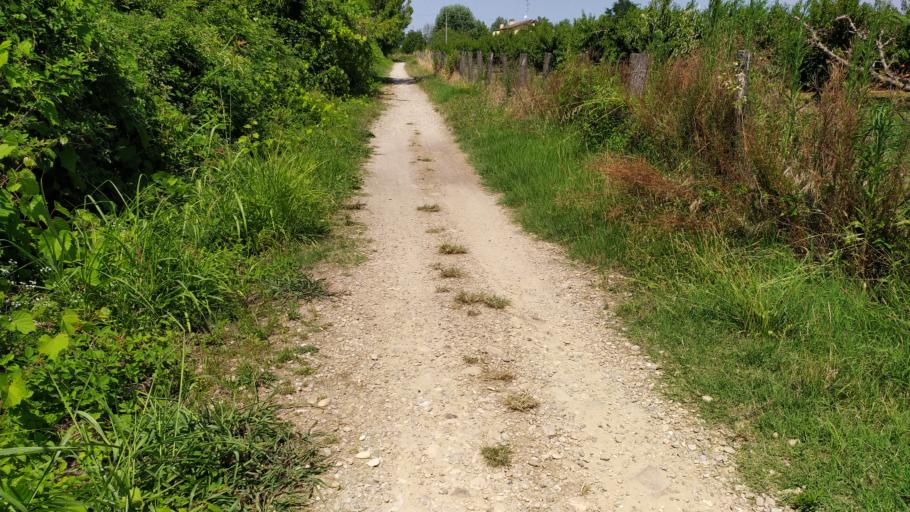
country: IT
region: Emilia-Romagna
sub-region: Forli-Cesena
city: Castrocaro Terme e Terra del Sole
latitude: 44.2017
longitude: 11.9910
